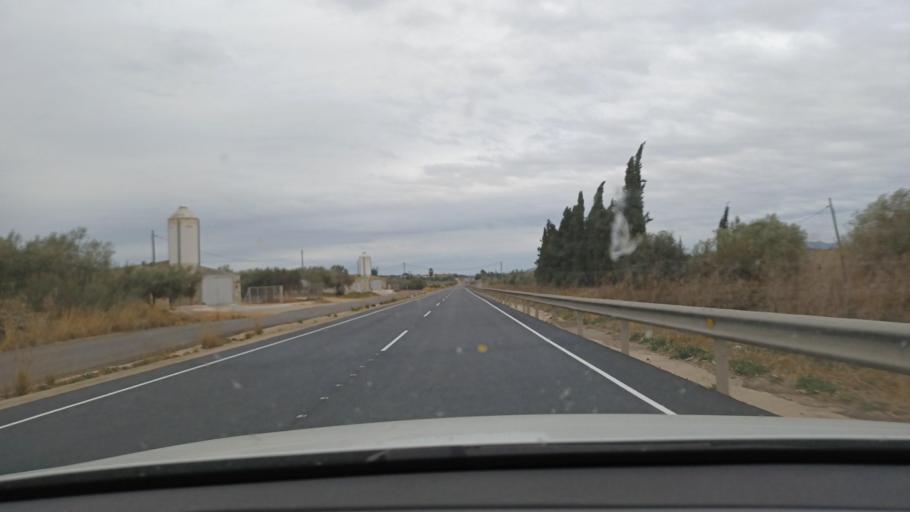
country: ES
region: Valencia
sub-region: Provincia de Castello
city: Traiguera
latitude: 40.5377
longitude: 0.3092
